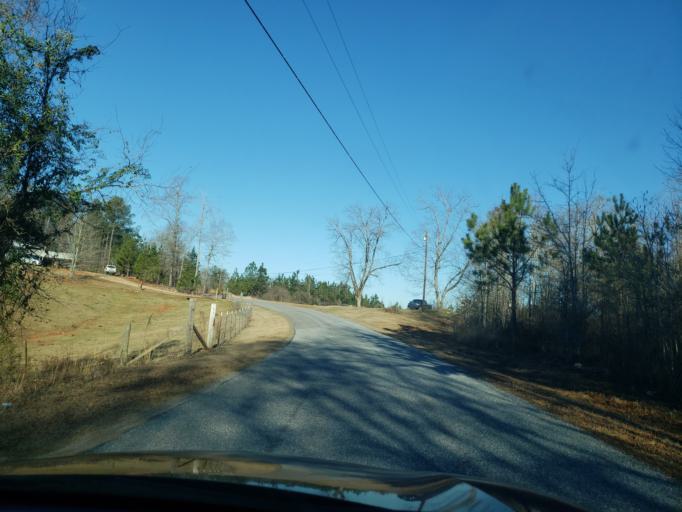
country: US
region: Alabama
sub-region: Elmore County
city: Tallassee
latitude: 32.6637
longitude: -85.8607
